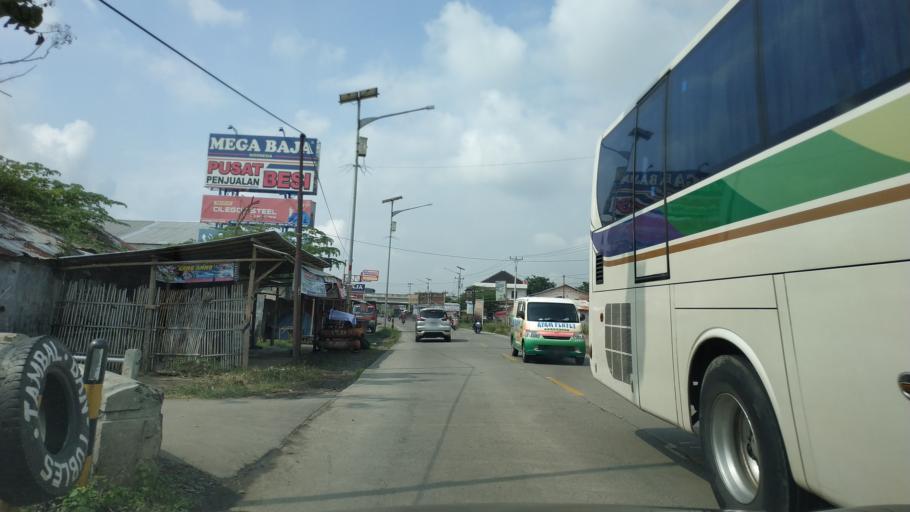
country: ID
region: Central Java
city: Ketanggungan
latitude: -6.8971
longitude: 108.8866
